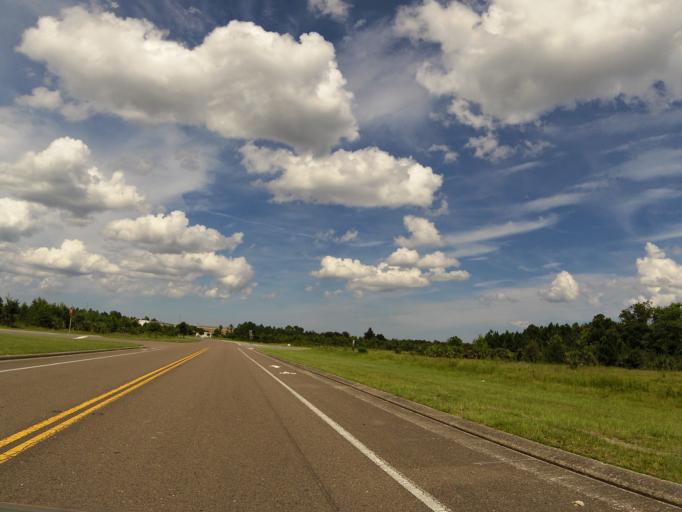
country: US
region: Florida
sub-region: Duval County
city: Jacksonville
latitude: 30.4183
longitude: -81.6385
